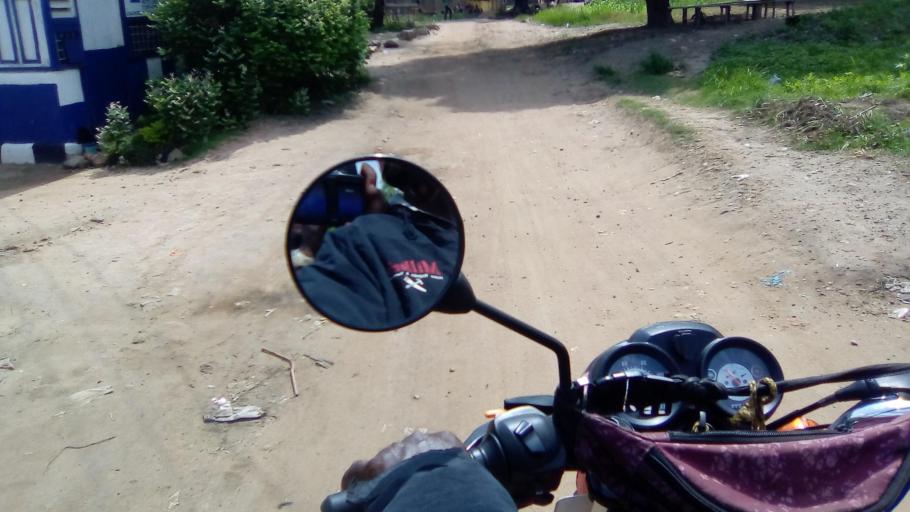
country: SL
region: Southern Province
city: Bo
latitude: 7.9489
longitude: -11.7235
